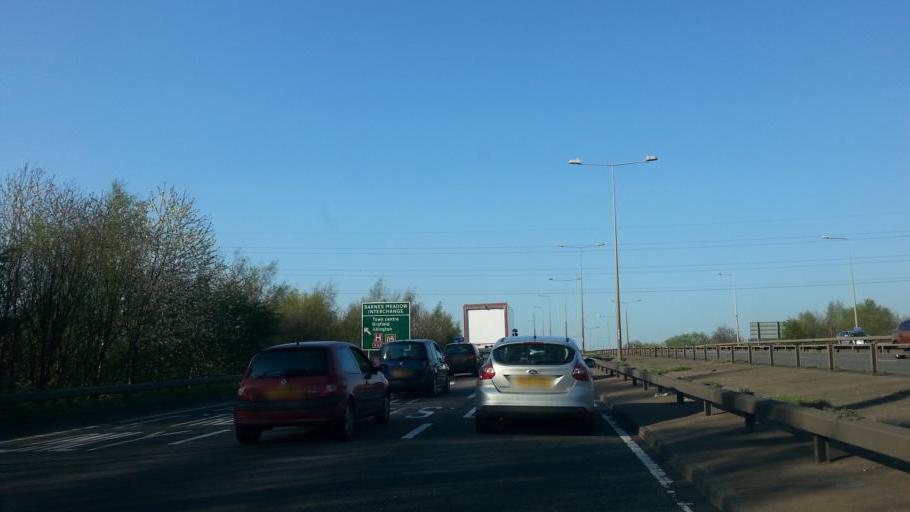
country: GB
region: England
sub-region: Northamptonshire
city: Hardingstone
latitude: 52.2252
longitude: -0.8732
